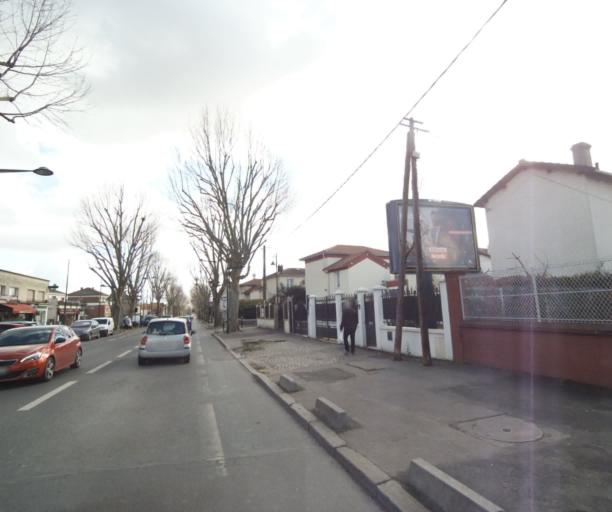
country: FR
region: Ile-de-France
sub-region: Departement de Seine-Saint-Denis
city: Villetaneuse
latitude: 48.9519
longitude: 2.3385
